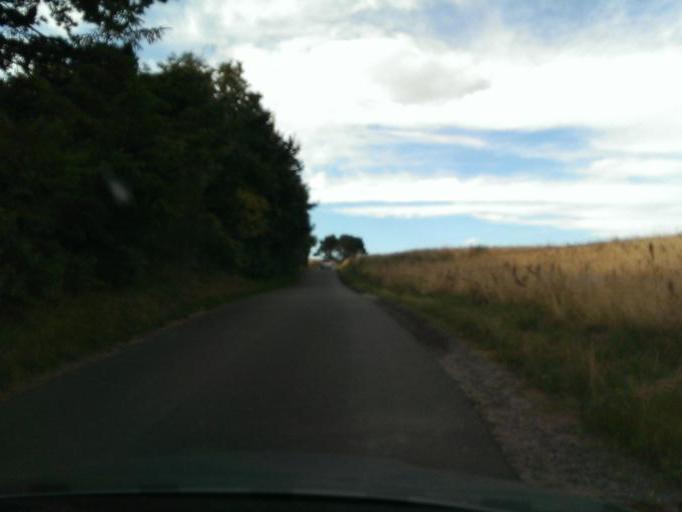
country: DK
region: Central Jutland
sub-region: Syddjurs Kommune
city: Ronde
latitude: 56.1086
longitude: 10.5058
